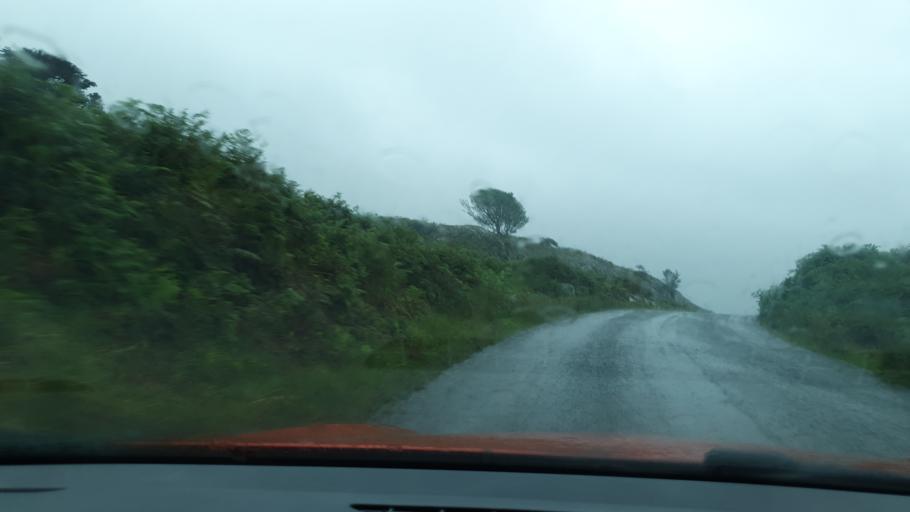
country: GB
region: England
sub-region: Cumbria
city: Millom
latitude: 54.3191
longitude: -3.2339
